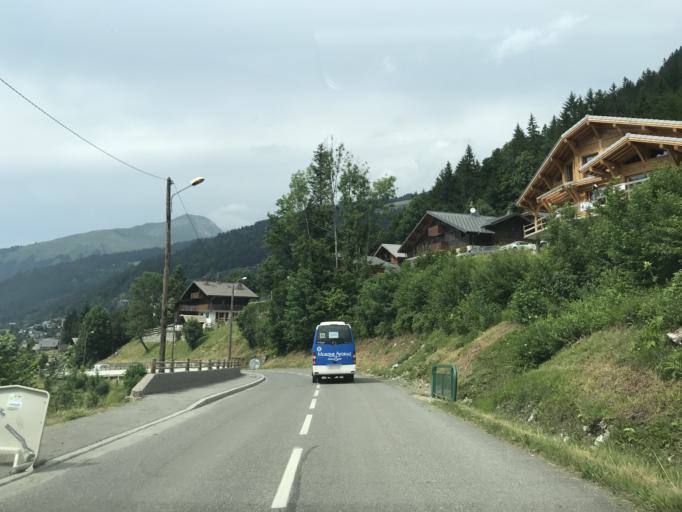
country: FR
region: Rhone-Alpes
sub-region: Departement de la Haute-Savoie
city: Morzine
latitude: 46.1724
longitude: 6.7122
